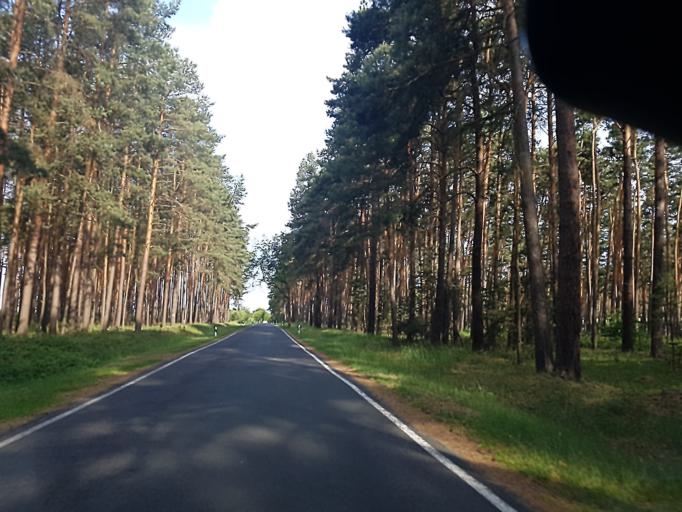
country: DE
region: Brandenburg
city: Belzig
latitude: 52.0727
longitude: 12.5380
